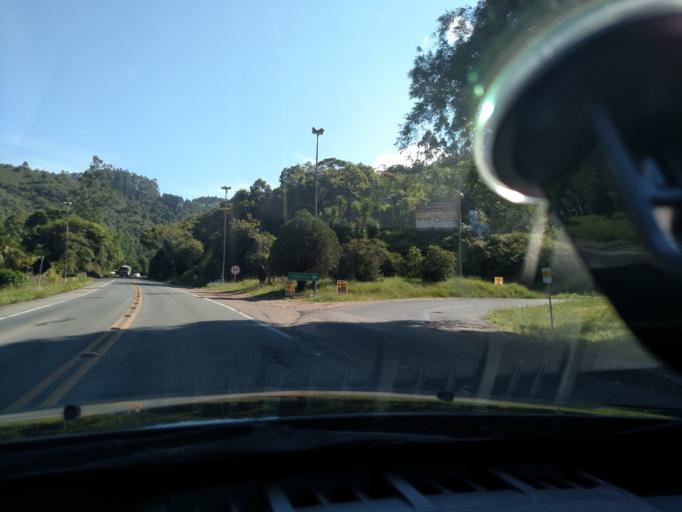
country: BR
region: Santa Catarina
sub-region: Ibirama
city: Ibirama
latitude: -27.0792
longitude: -49.4991
